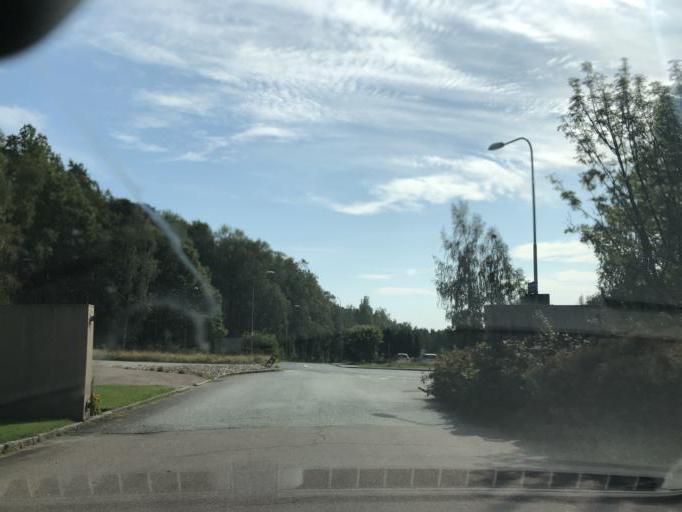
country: SE
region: Vaestra Goetaland
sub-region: Goteborg
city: Goeteborg
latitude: 57.7636
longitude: 11.9770
